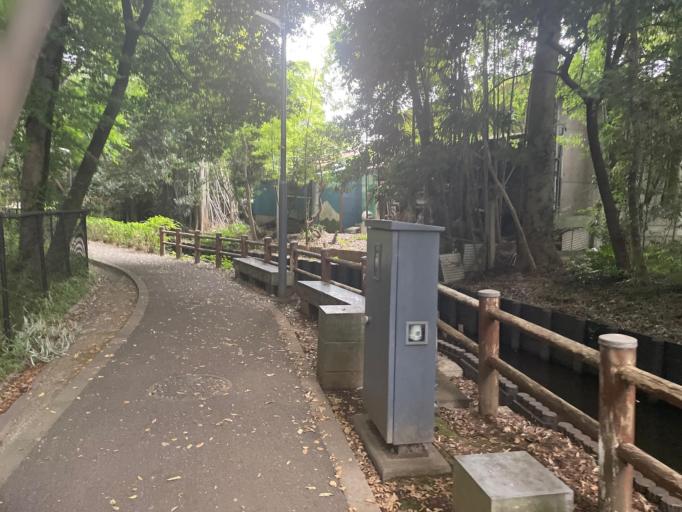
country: JP
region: Tokyo
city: Higashimurayama-shi
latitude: 35.7484
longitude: 139.4905
